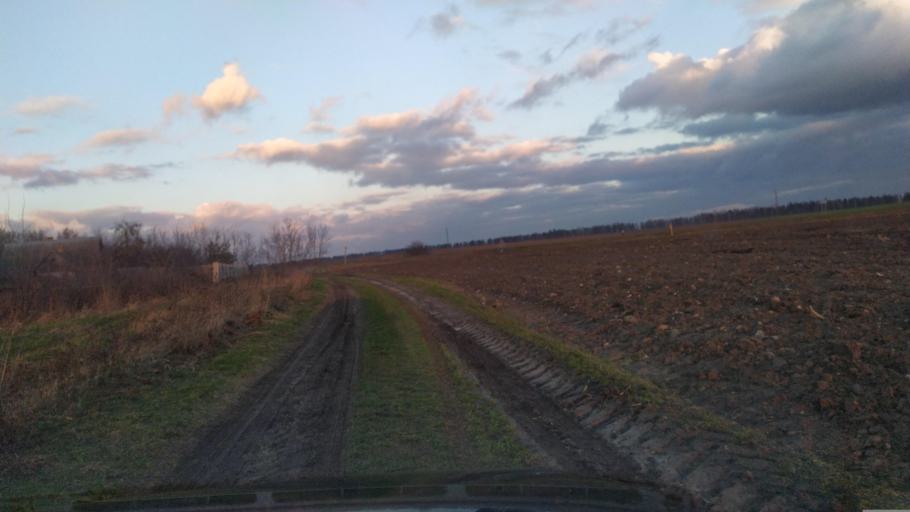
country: BY
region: Brest
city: Kamyanyets
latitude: 52.4238
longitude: 23.7697
